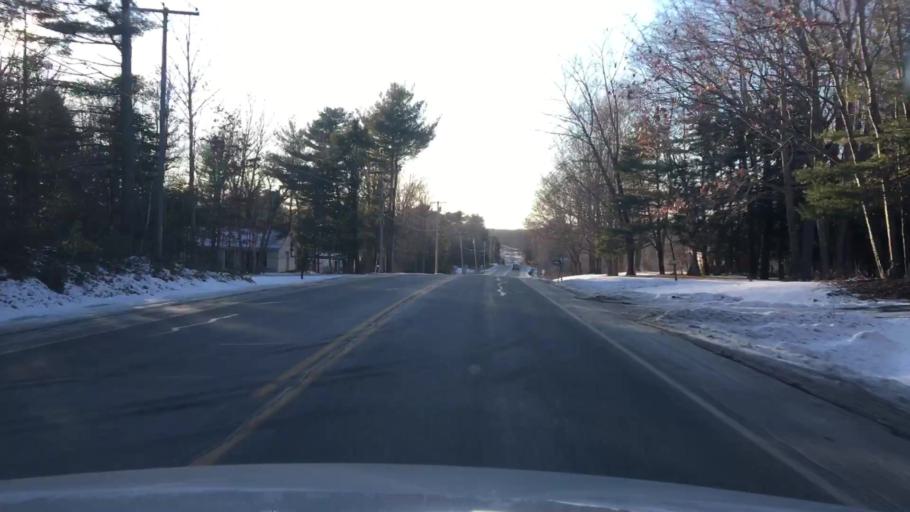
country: US
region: Maine
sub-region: Penobscot County
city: Eddington
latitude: 44.8280
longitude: -68.6829
